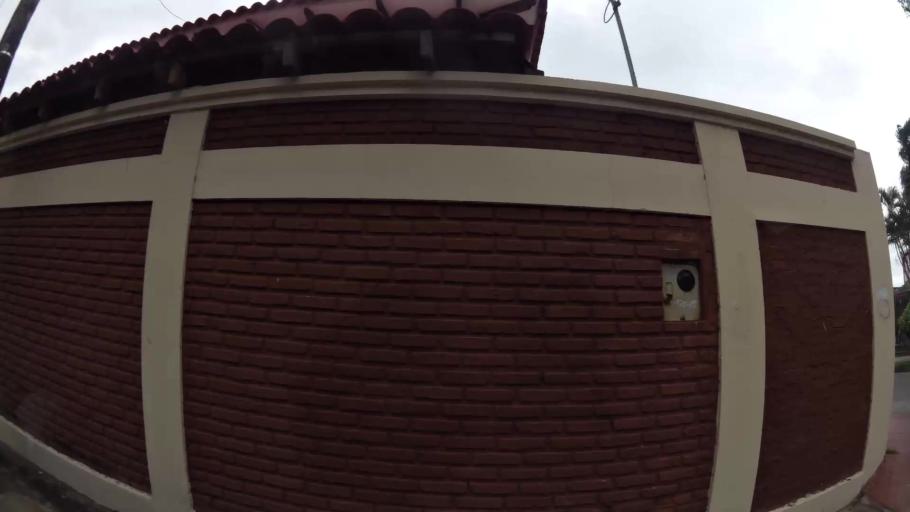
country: BO
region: Santa Cruz
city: Santa Cruz de la Sierra
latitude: -17.7723
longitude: -63.1637
